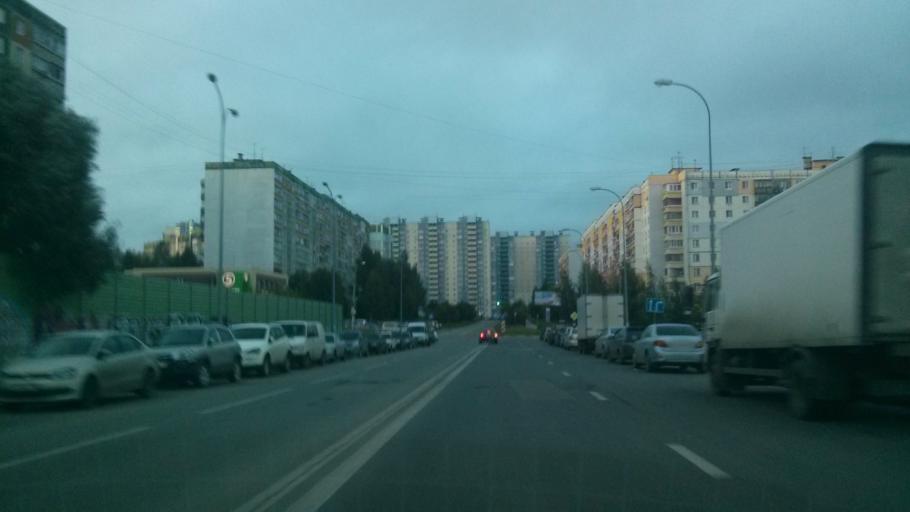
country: RU
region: Nizjnij Novgorod
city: Afonino
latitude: 56.2887
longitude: 44.0681
